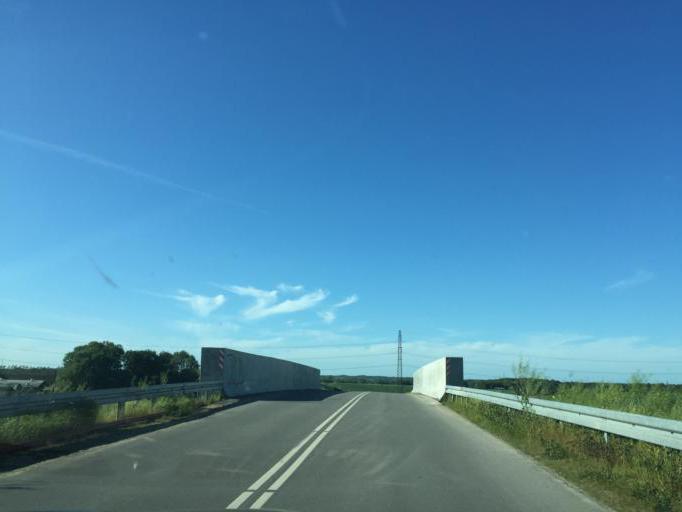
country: DK
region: Zealand
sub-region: Ringsted Kommune
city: Ringsted
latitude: 55.4481
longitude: 11.8816
